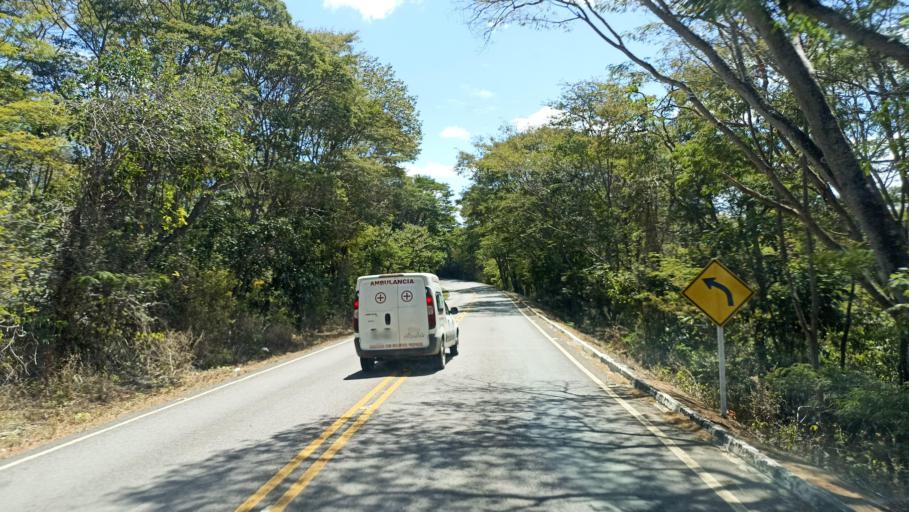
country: BR
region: Bahia
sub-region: Andarai
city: Vera Cruz
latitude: -12.7637
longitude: -41.3254
